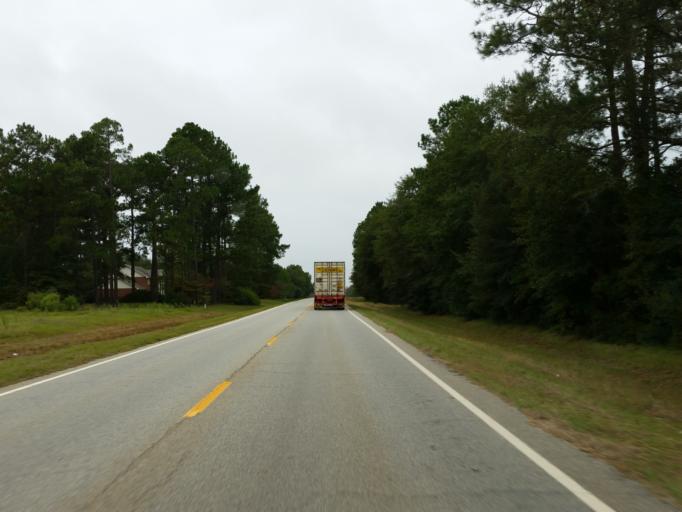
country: US
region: Georgia
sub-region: Berrien County
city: Ray City
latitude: 31.0864
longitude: -83.2398
